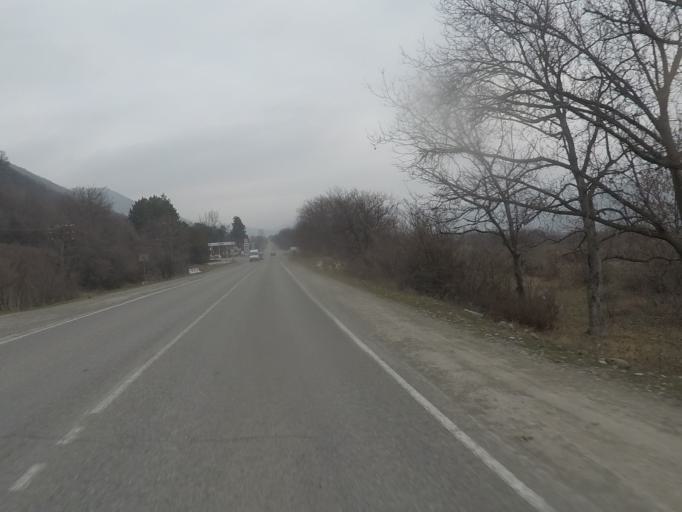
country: GE
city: Zhinvali
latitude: 42.0605
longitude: 44.7449
